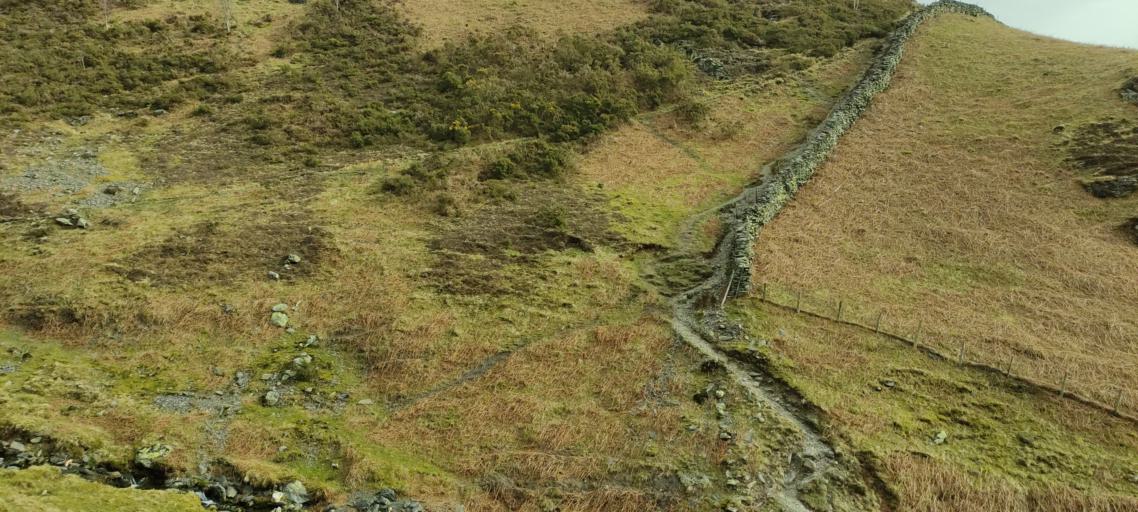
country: GB
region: England
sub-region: Cumbria
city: Keswick
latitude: 54.6300
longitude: -3.0386
